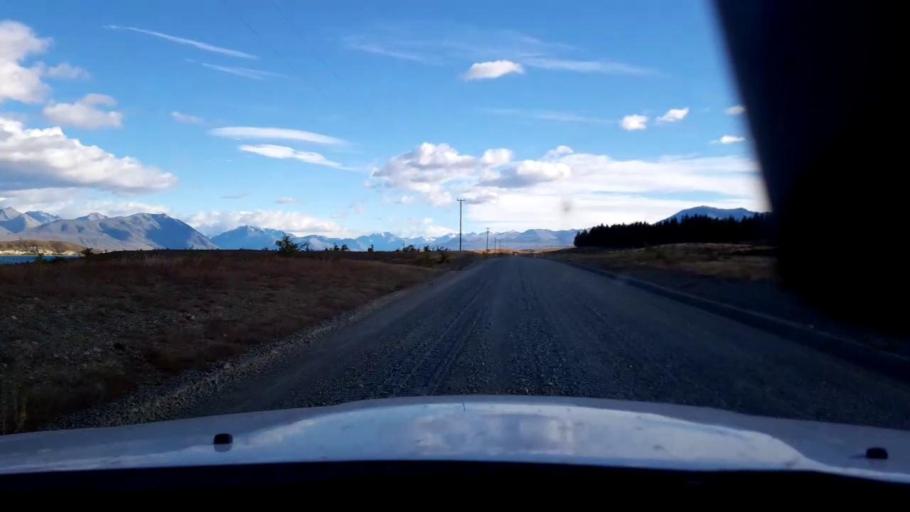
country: NZ
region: Canterbury
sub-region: Timaru District
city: Pleasant Point
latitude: -43.9879
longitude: 170.5044
